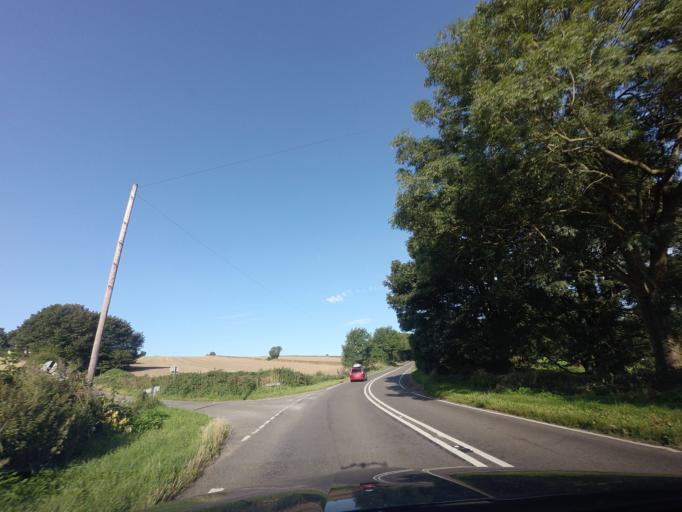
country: GB
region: England
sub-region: Derbyshire
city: Dronfield
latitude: 53.2317
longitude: -1.5239
